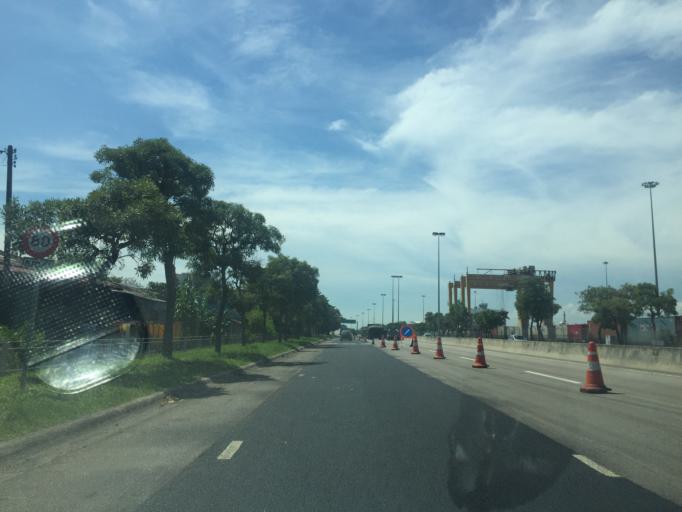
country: MY
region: Penang
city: Butterworth
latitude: 5.4139
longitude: 100.3706
